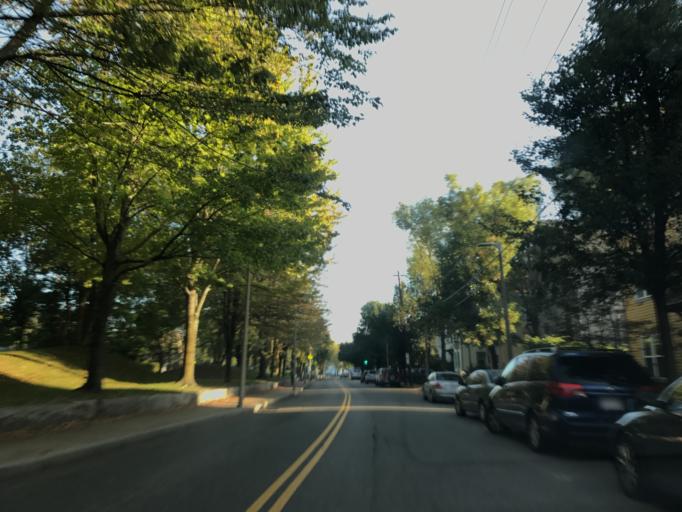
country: US
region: Massachusetts
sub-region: Suffolk County
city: Jamaica Plain
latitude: 42.3125
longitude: -71.1057
